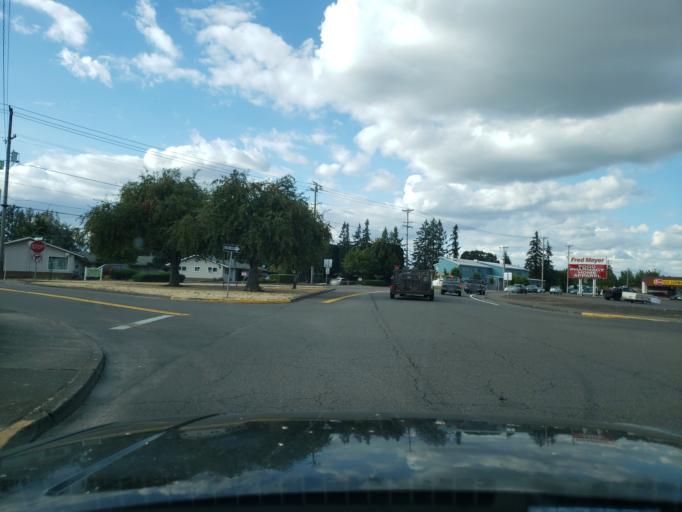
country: US
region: Oregon
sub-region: Marion County
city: Keizer
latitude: 44.9685
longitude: -123.0320
